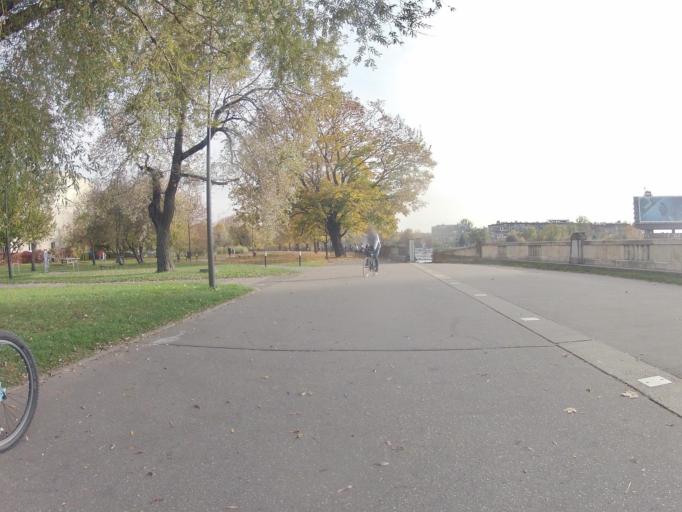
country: PL
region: Lesser Poland Voivodeship
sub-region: Krakow
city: Krakow
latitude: 50.0473
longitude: 19.9375
